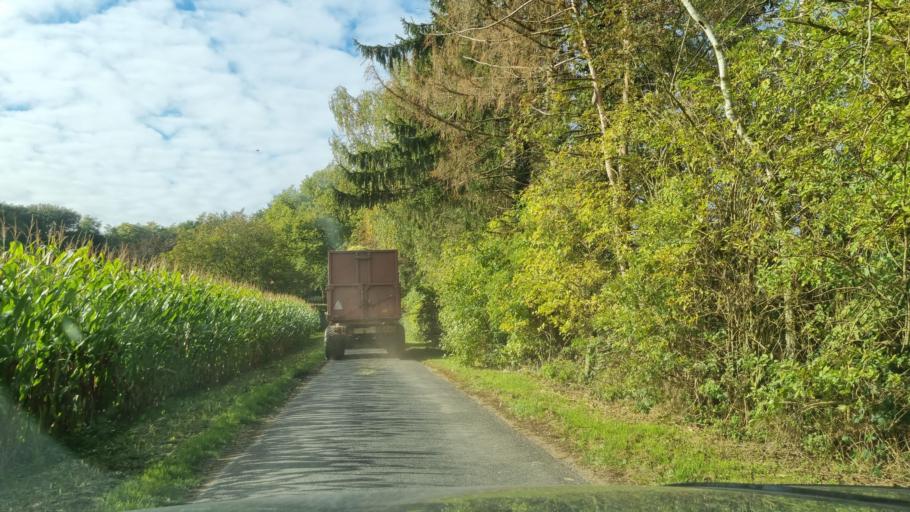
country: DE
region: North Rhine-Westphalia
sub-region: Regierungsbezirk Dusseldorf
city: Kranenburg
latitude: 51.7622
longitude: 6.0304
